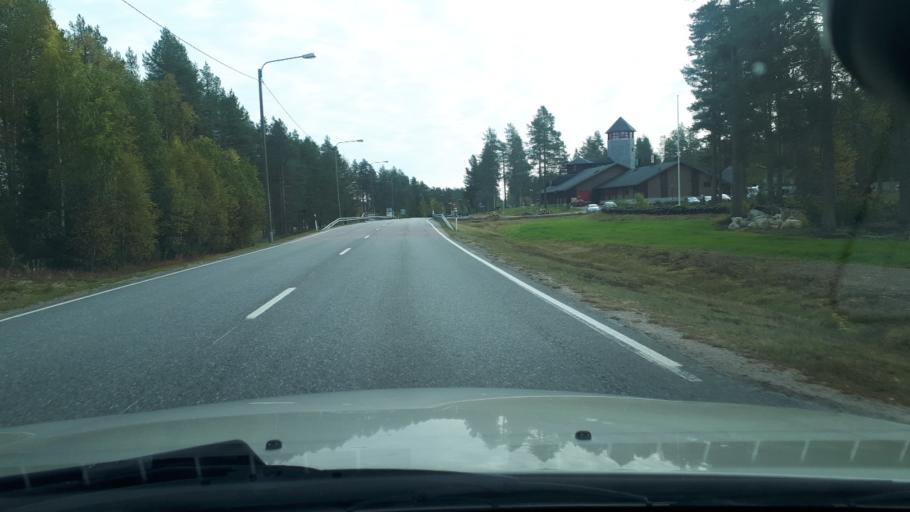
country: FI
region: Lapland
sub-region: Rovaniemi
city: Ranua
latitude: 65.9450
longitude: 26.4636
